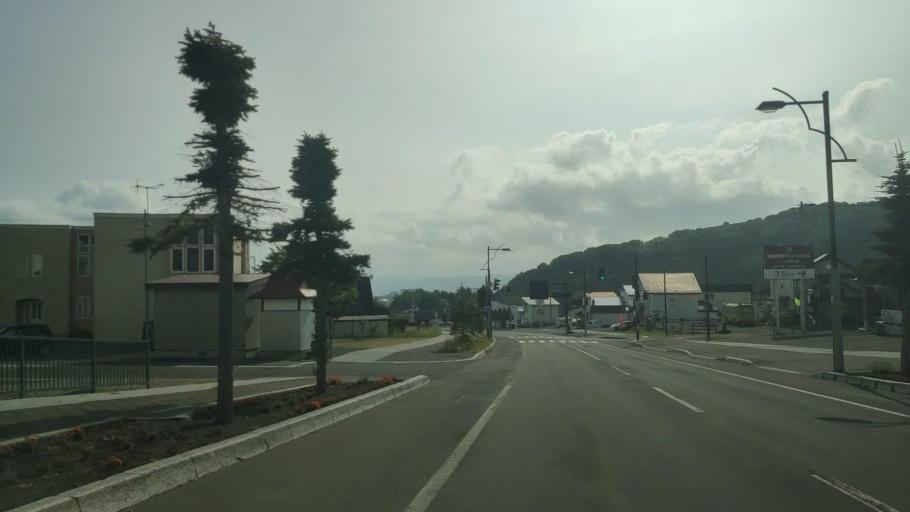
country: JP
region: Hokkaido
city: Shimo-furano
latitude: 43.3435
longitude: 142.3666
